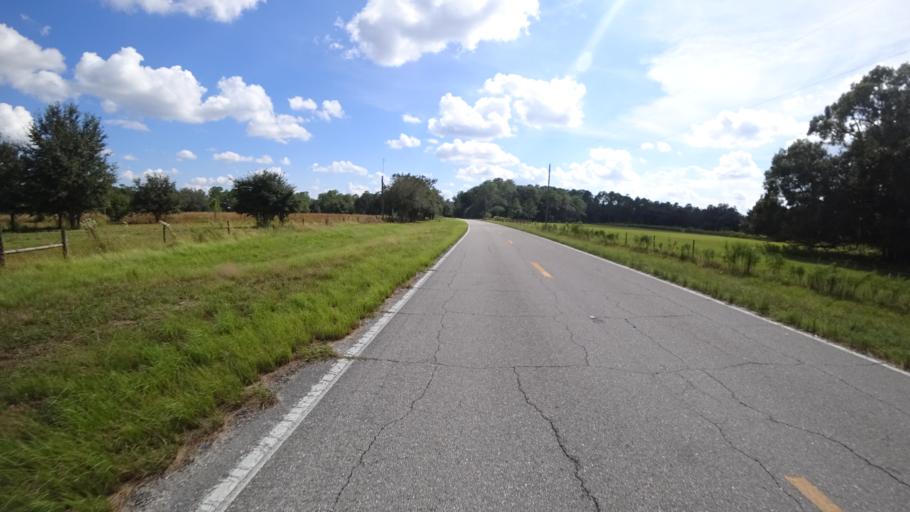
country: US
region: Florida
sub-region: Hardee County
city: Wauchula
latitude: 27.4759
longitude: -82.0795
